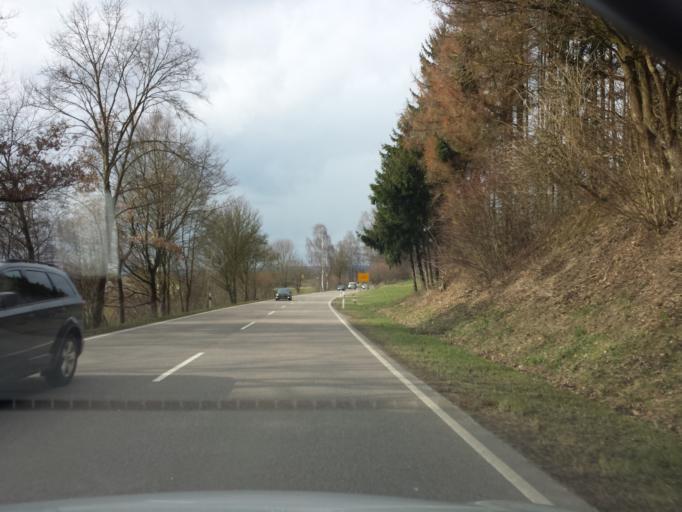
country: DE
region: Baden-Wuerttemberg
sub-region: Tuebingen Region
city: Achstetten
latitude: 48.2566
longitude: 9.9103
